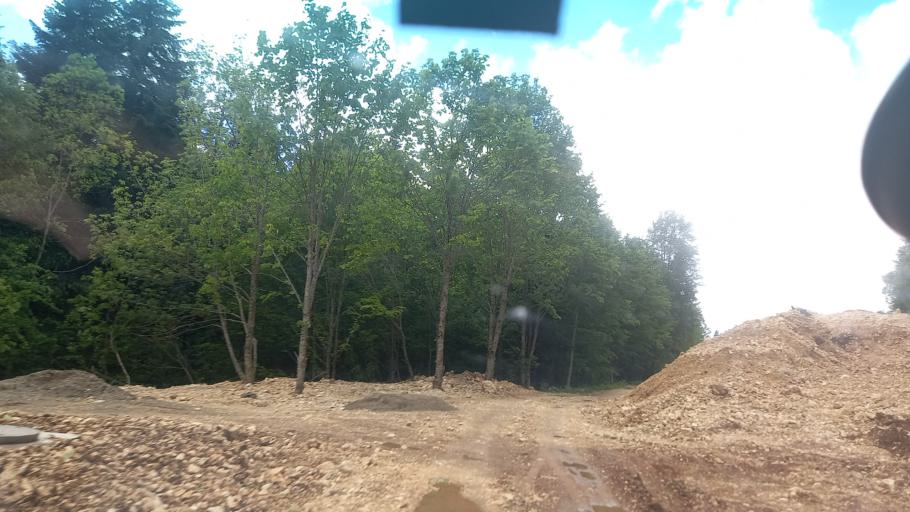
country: RU
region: Krasnodarskiy
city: Neftegorsk
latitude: 44.0551
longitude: 39.8205
